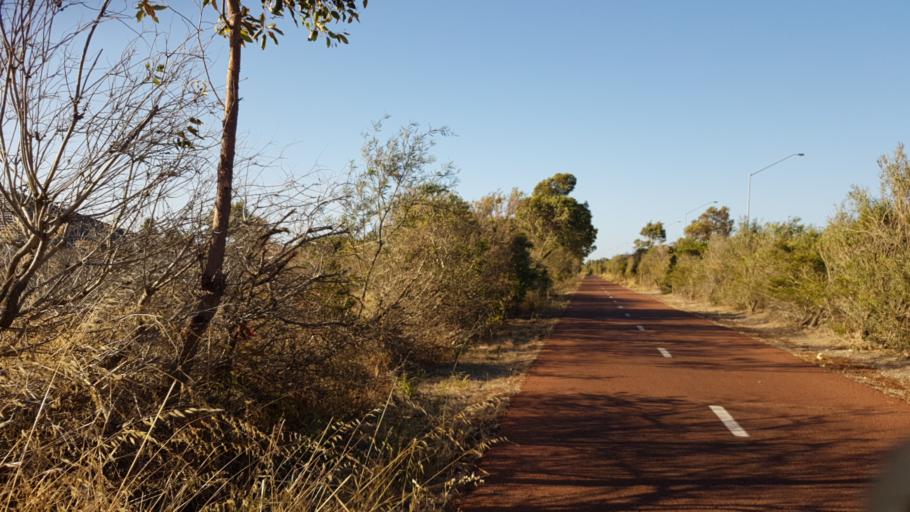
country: AU
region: Western Australia
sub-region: Kwinana
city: Bertram
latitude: -32.2504
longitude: 115.8523
